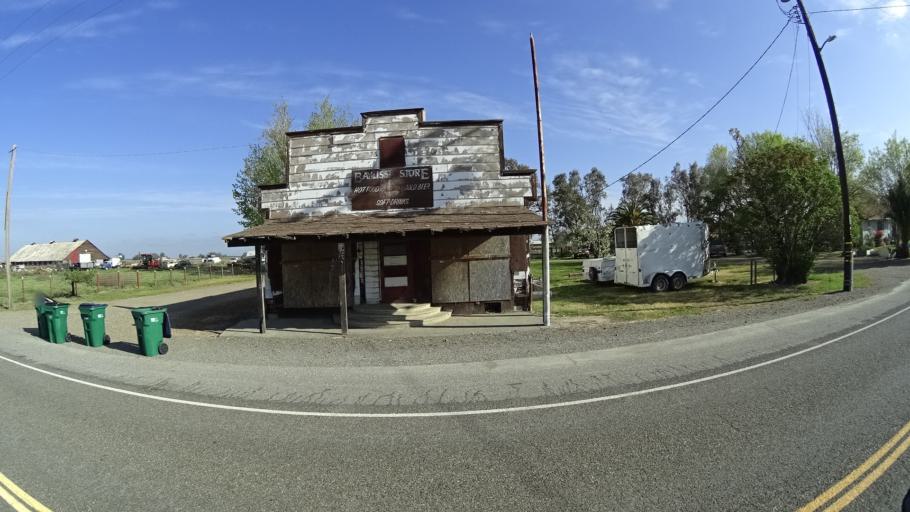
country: US
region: California
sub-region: Glenn County
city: Willows
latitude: 39.5825
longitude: -122.0474
